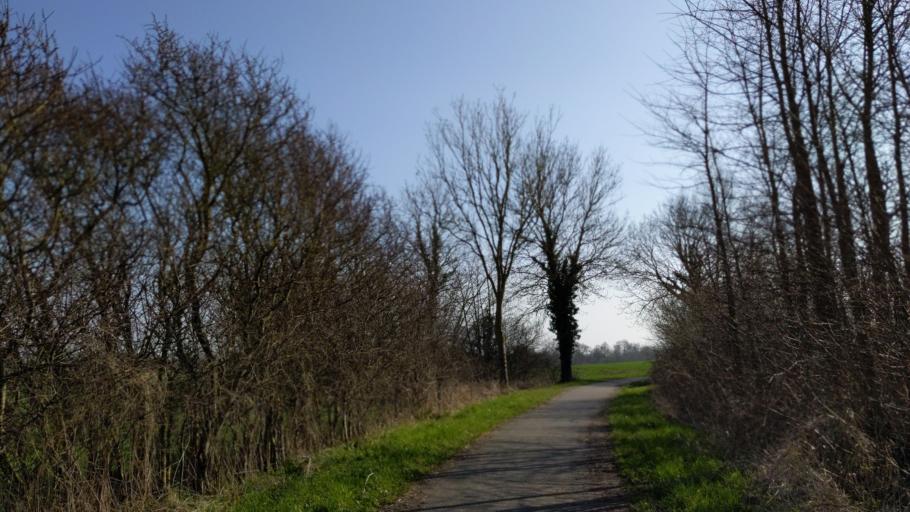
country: DE
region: Schleswig-Holstein
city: Altenkrempe
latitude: 54.1238
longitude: 10.8491
